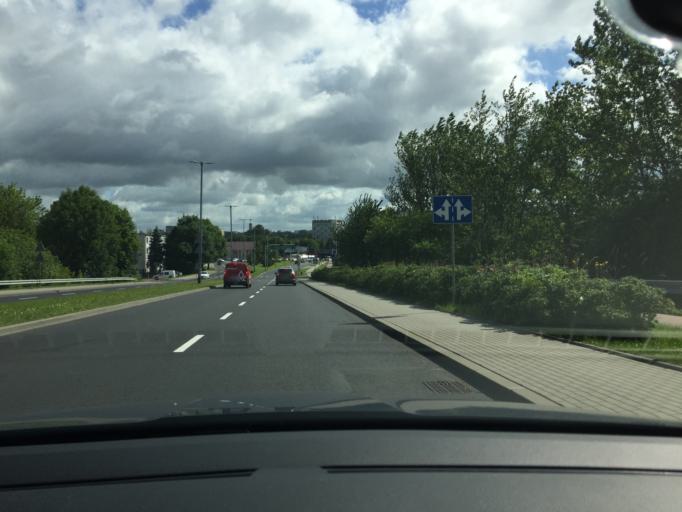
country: PL
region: West Pomeranian Voivodeship
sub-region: Koszalin
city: Koszalin
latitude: 54.1926
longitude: 16.1650
